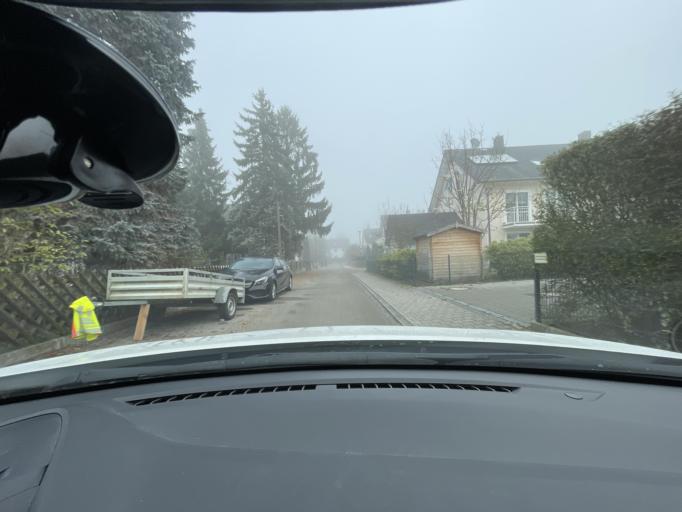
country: DE
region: Bavaria
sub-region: Upper Bavaria
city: Maisach
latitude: 48.2154
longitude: 11.2655
